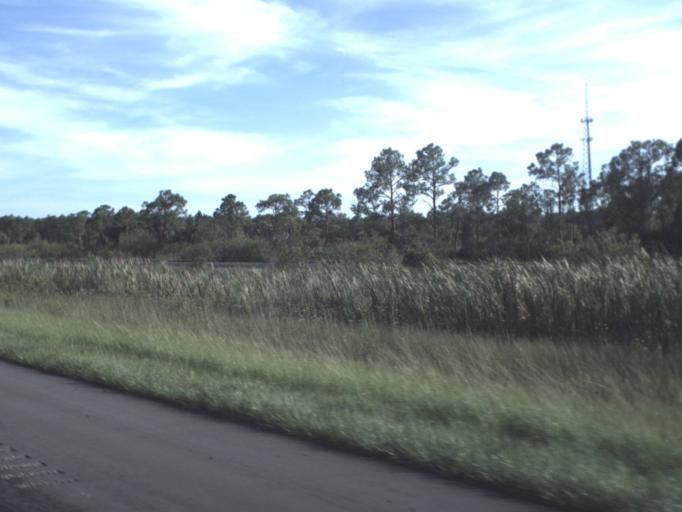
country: US
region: Florida
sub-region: Lee County
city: Suncoast Estates
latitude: 26.8146
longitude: -81.9367
